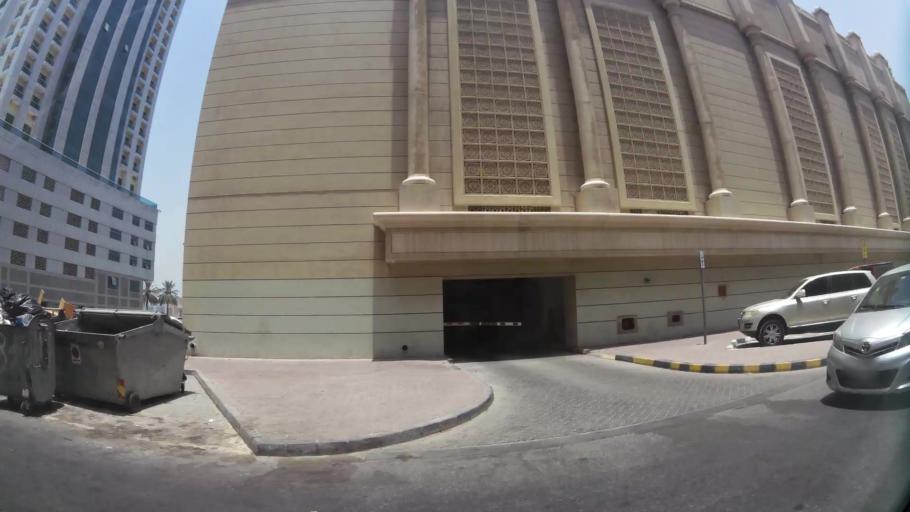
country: AE
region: Ash Shariqah
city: Sharjah
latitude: 25.3313
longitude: 55.3754
